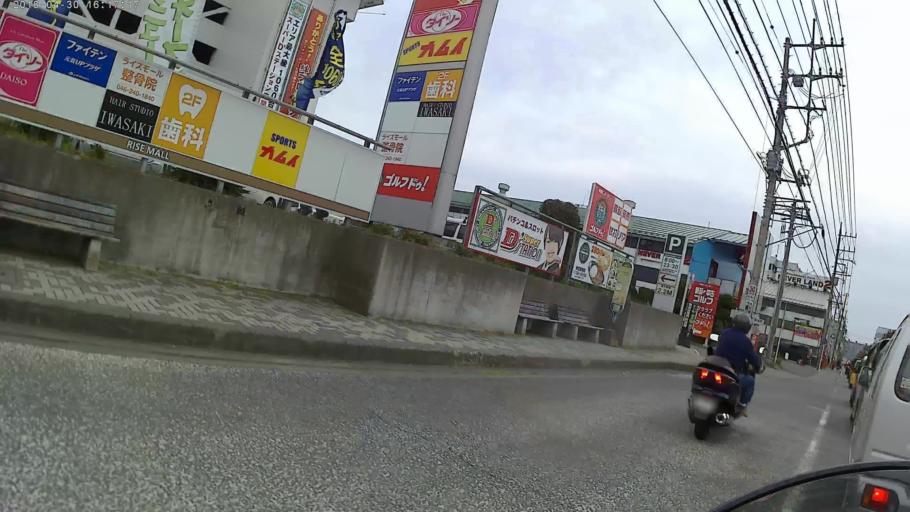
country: JP
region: Kanagawa
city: Minami-rinkan
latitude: 35.4805
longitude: 139.4317
